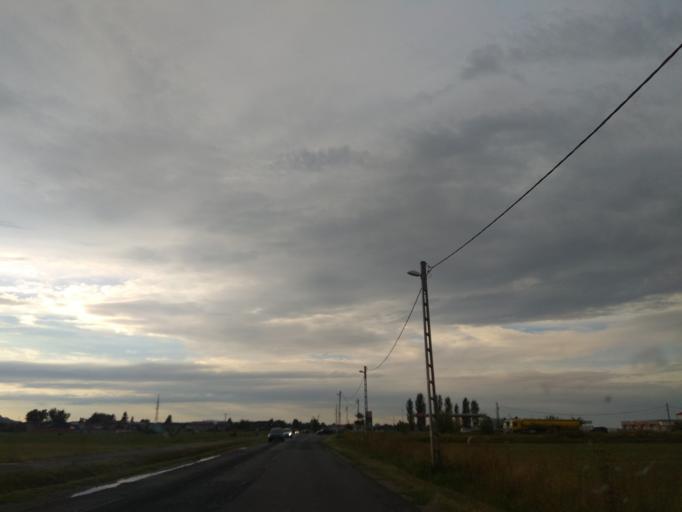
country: HU
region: Borsod-Abauj-Zemplen
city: Miskolc
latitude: 48.0814
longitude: 20.8206
